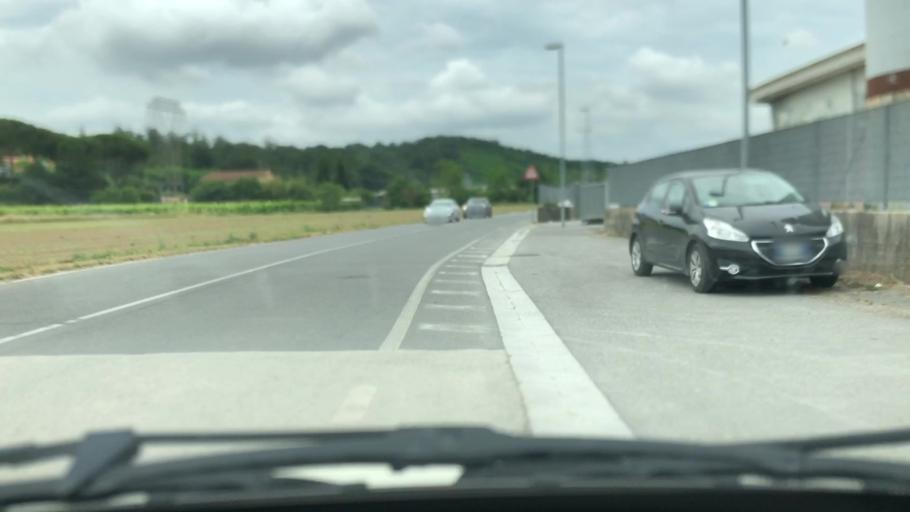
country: IT
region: Tuscany
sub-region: Province of Pisa
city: Calcinaia
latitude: 43.6926
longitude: 10.6259
